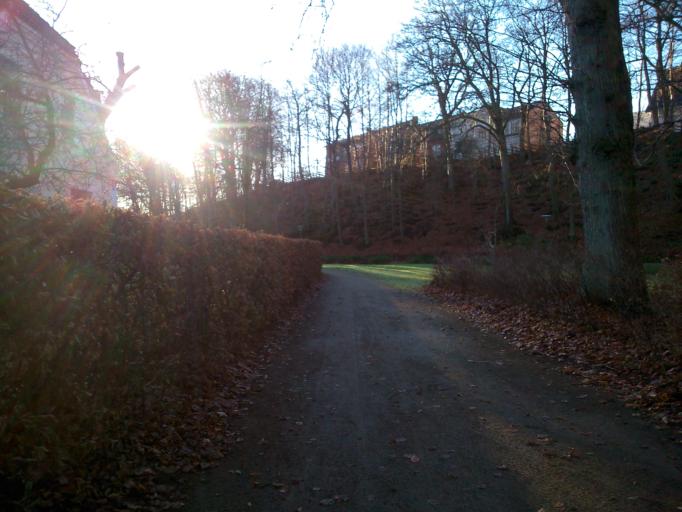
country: DK
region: Central Jutland
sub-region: Holstebro Kommune
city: Holstebro
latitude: 56.3598
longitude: 8.6244
